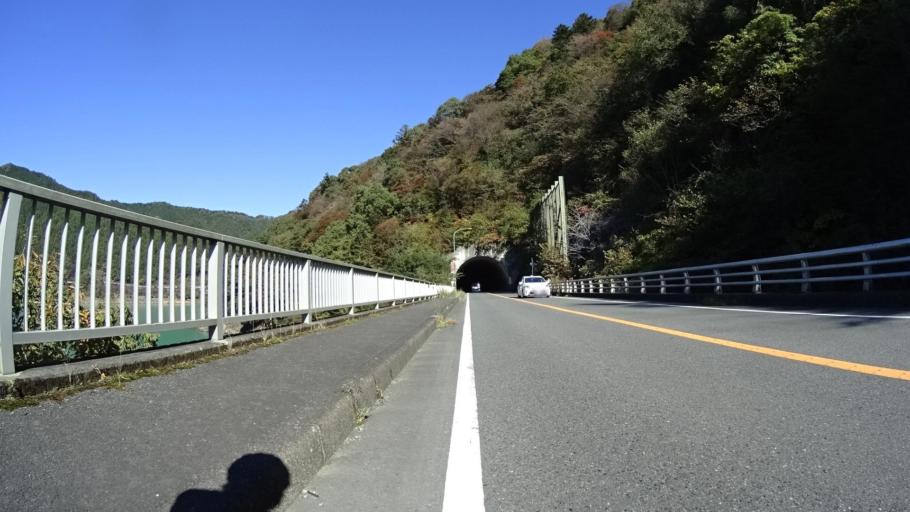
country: JP
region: Tokyo
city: Hachioji
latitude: 35.5355
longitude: 139.2421
